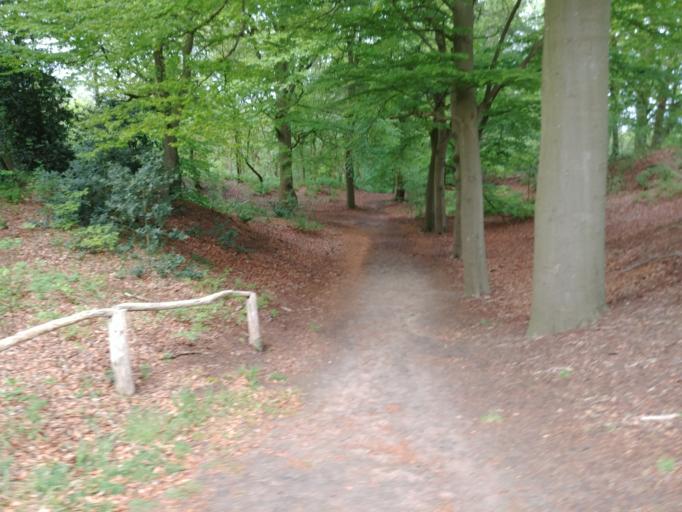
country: NL
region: Overijssel
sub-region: Gemeente Dalfsen
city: Dalfsen
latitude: 52.5155
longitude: 6.3499
